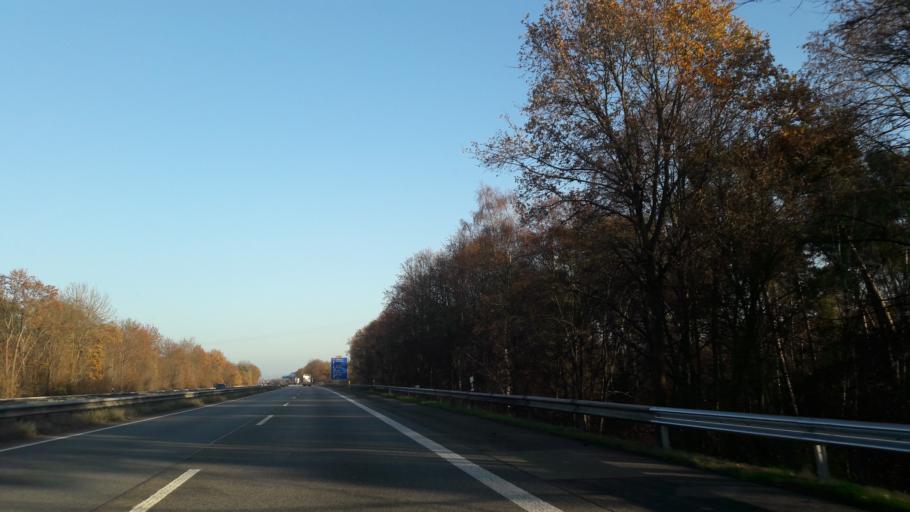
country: DE
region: Rheinland-Pfalz
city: Dudenhofen
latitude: 49.3532
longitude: 8.4026
